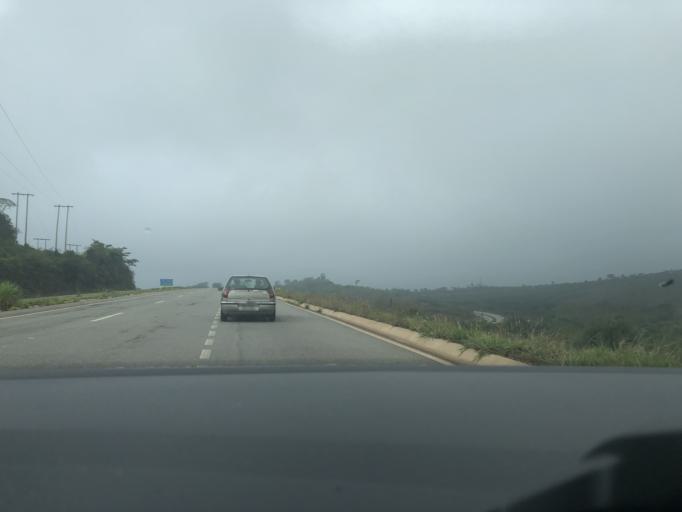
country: BR
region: Minas Gerais
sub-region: Congonhas
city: Congonhas
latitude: -20.5856
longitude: -43.9454
